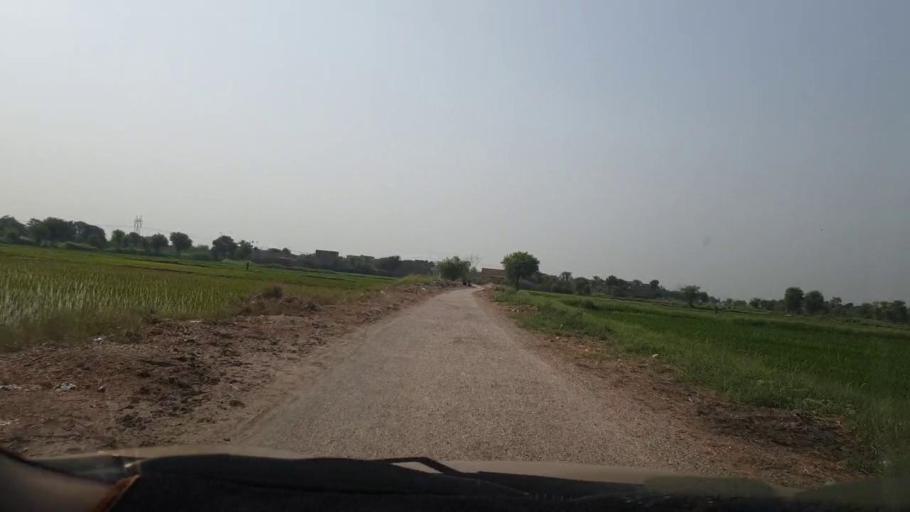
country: PK
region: Sindh
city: Goth Garelo
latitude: 27.4364
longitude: 68.0427
